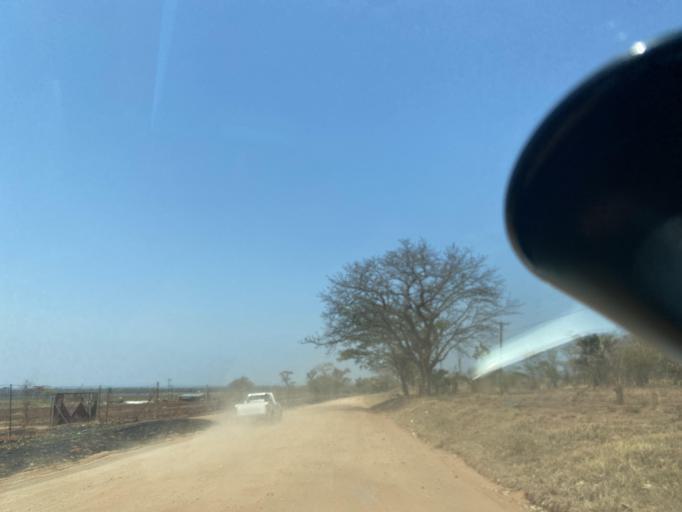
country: ZM
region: Lusaka
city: Kafue
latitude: -15.5469
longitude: 28.0695
